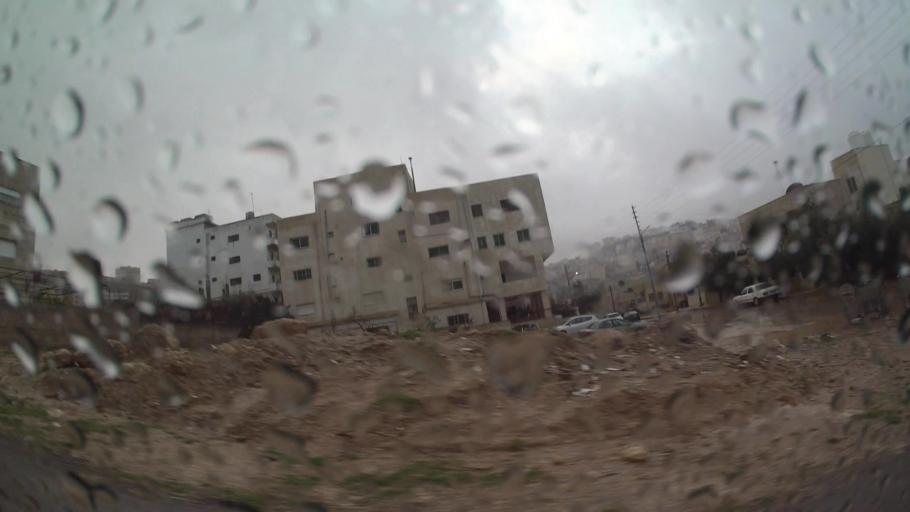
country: JO
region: Amman
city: Al Jubayhah
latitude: 32.0326
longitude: 35.8425
